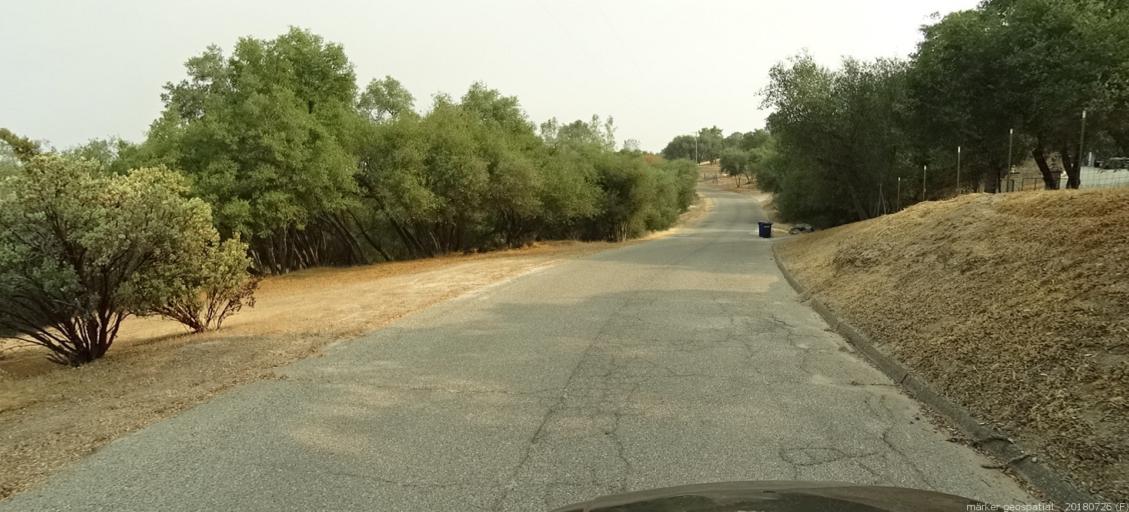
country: US
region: California
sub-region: Madera County
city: Coarsegold
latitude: 37.2155
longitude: -119.7154
